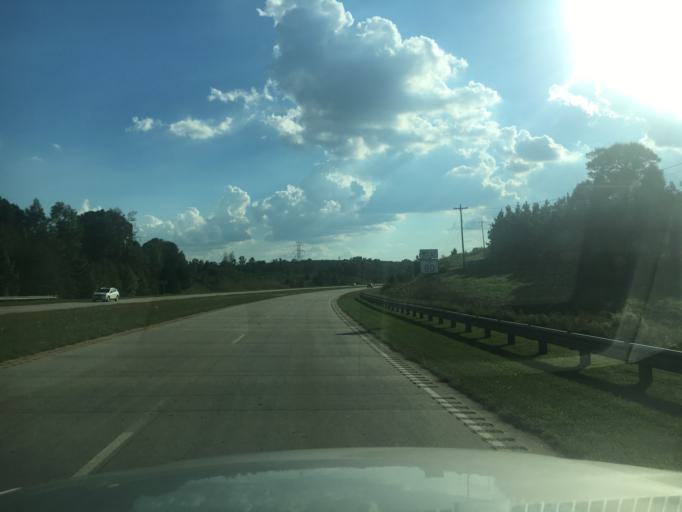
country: US
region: South Carolina
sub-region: Greenville County
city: Greer
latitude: 34.9282
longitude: -82.1919
